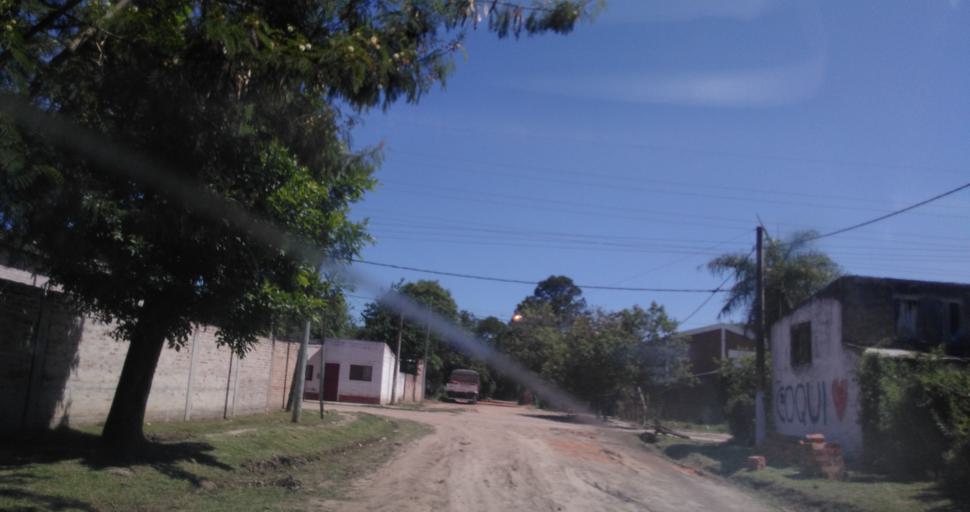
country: AR
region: Chaco
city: Resistencia
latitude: -27.4218
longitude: -58.9780
